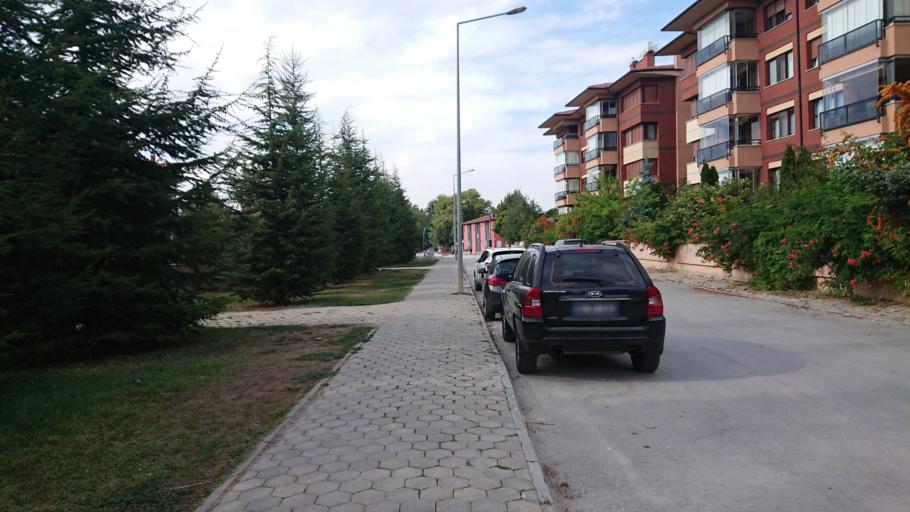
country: TR
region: Eskisehir
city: Eskisehir
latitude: 39.7673
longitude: 30.4966
